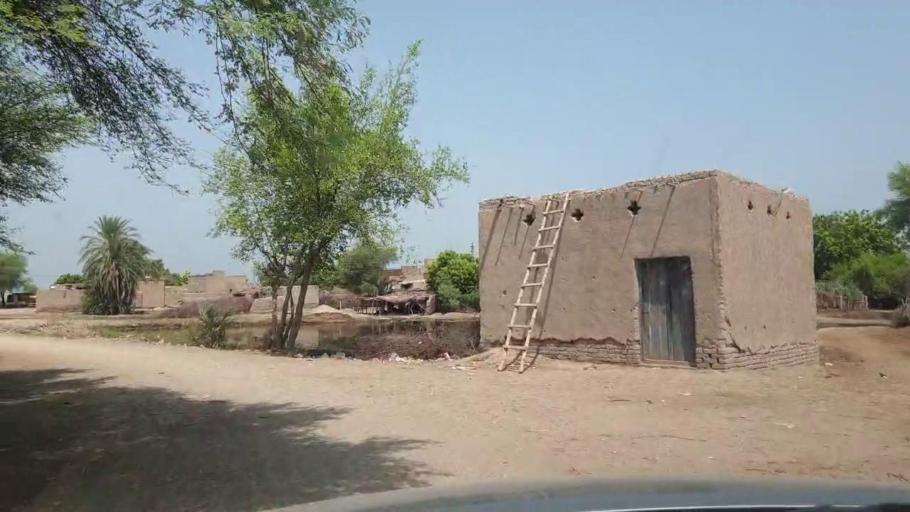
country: PK
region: Sindh
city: Madeji
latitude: 27.8092
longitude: 68.5194
